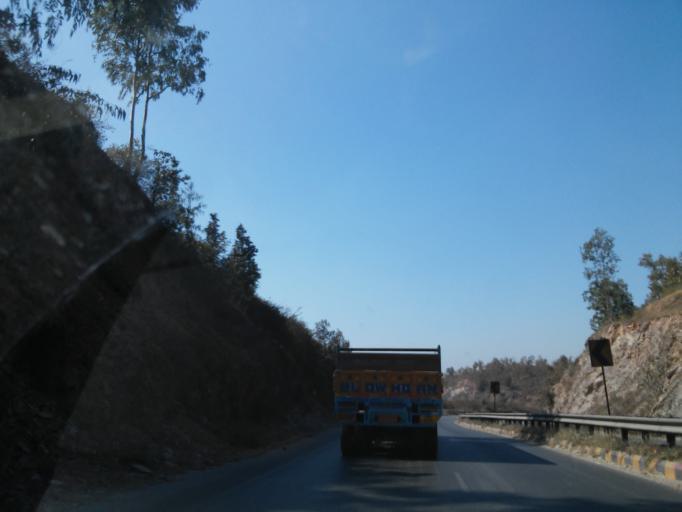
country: IN
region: Rajasthan
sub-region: Dungarpur
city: Dungarpur
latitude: 23.7720
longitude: 73.4950
